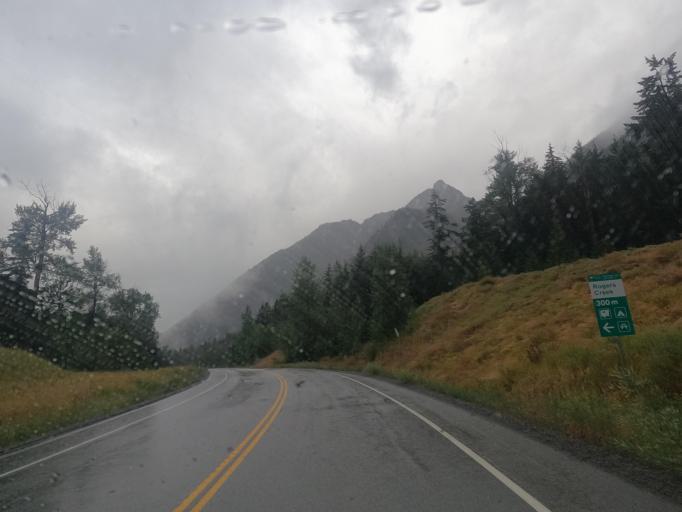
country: CA
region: British Columbia
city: Lillooet
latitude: 50.5338
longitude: -122.1523
